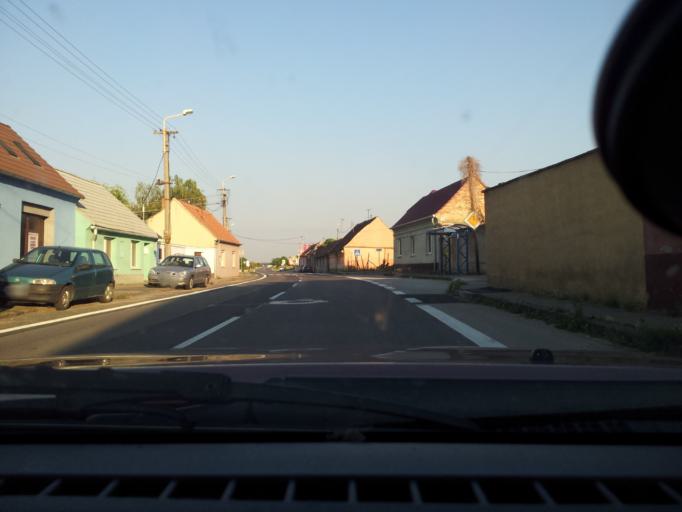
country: SK
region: Trnavsky
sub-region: Okres Skalica
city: Holic
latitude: 48.8087
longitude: 17.1677
